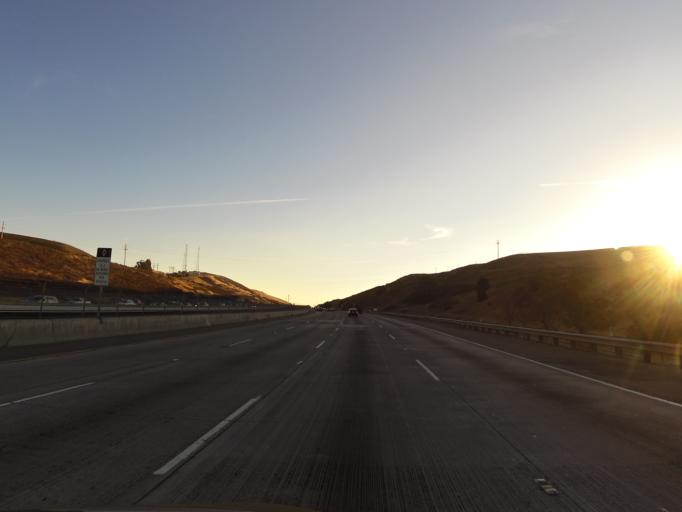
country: US
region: California
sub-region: Contra Costa County
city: Bay Point
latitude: 38.0145
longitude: -121.9949
